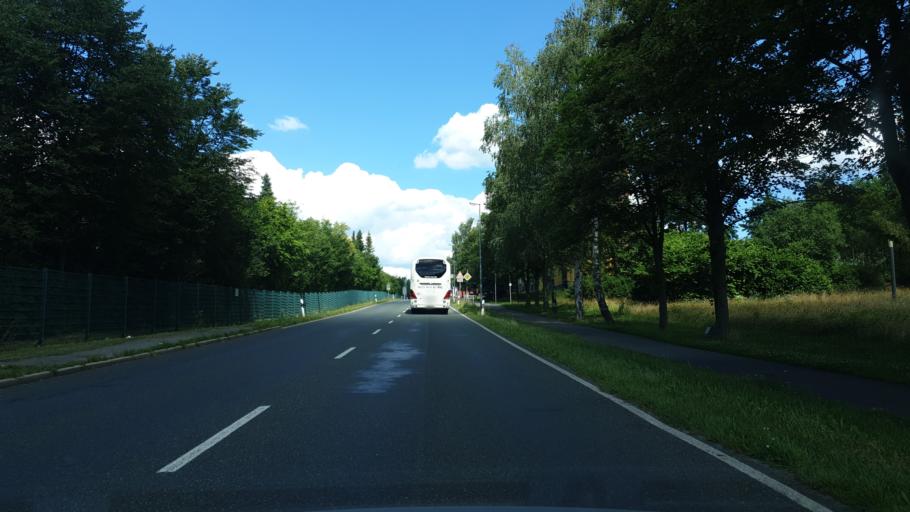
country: DE
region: Saxony
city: Marienberg
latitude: 50.6557
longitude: 13.1564
